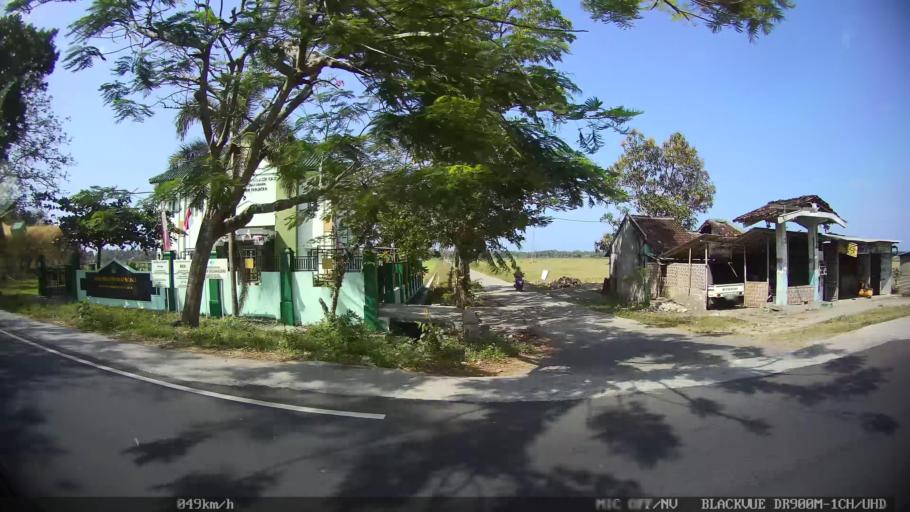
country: ID
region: Daerah Istimewa Yogyakarta
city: Srandakan
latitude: -7.8975
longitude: 110.1624
